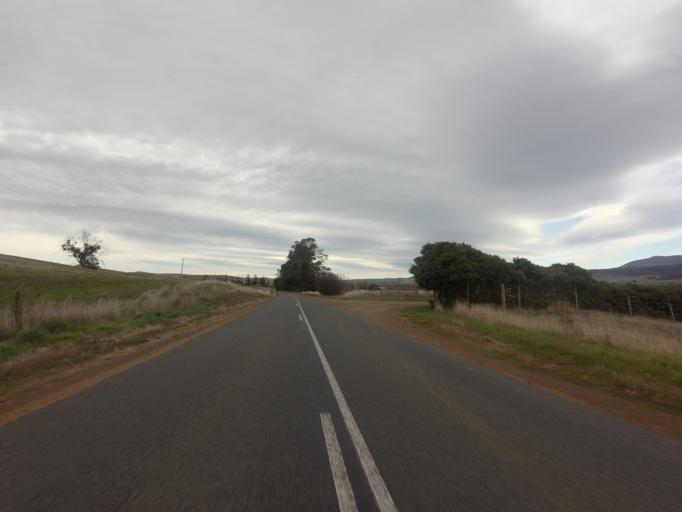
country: AU
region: Tasmania
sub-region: Derwent Valley
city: New Norfolk
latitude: -42.5152
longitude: 146.7453
